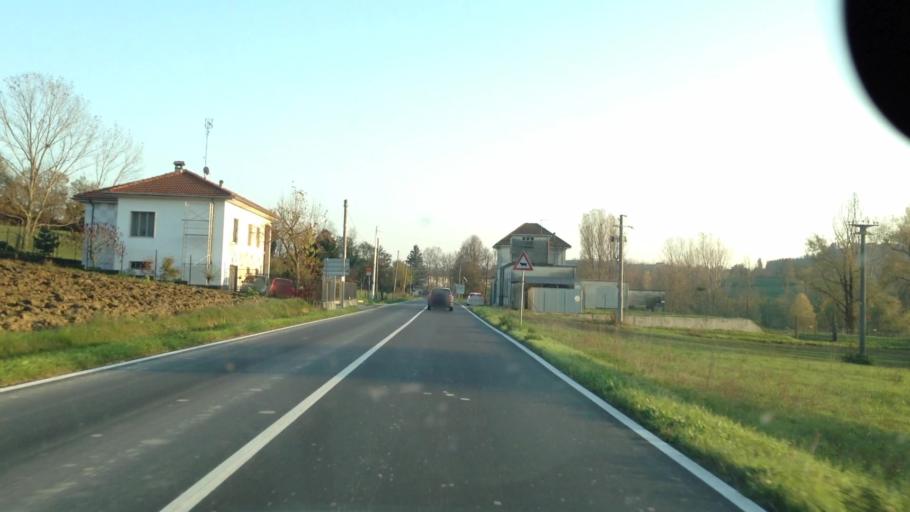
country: IT
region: Piedmont
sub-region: Provincia di Asti
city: Robella
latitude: 45.0955
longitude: 8.0861
